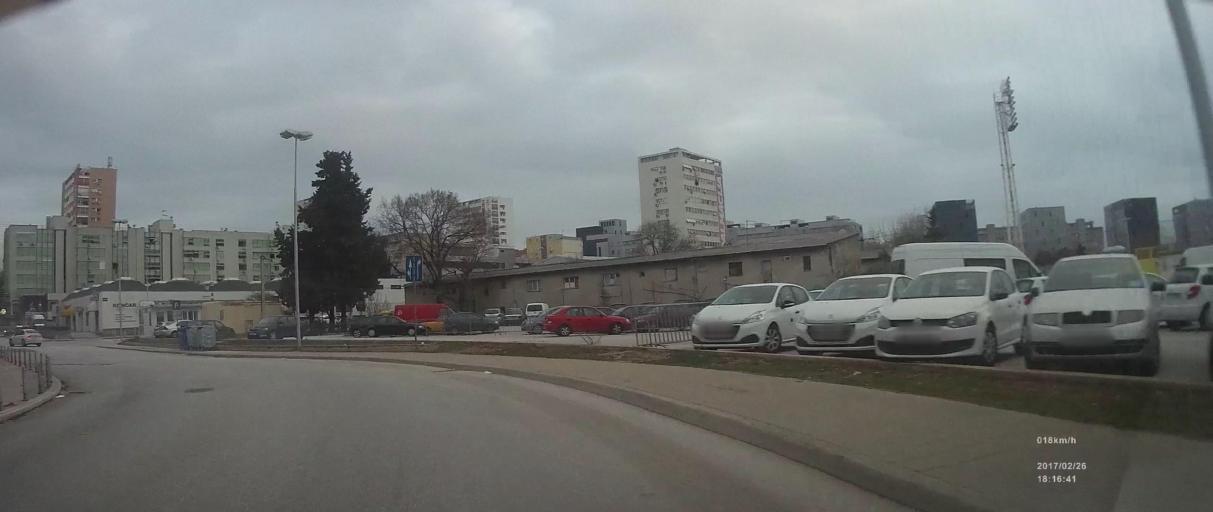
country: HR
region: Splitsko-Dalmatinska
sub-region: Grad Split
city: Split
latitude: 43.5194
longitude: 16.4456
